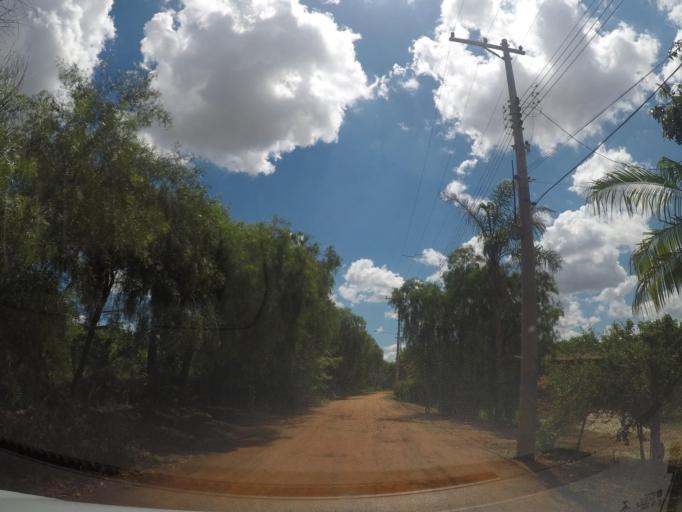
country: BR
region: Sao Paulo
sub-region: Sumare
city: Sumare
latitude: -22.8385
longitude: -47.2435
